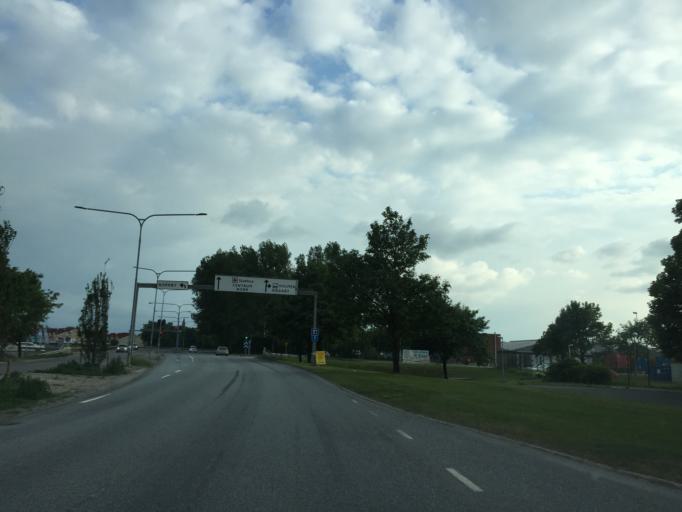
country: SE
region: OErebro
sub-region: Orebro Kommun
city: Orebro
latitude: 59.2896
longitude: 15.2238
